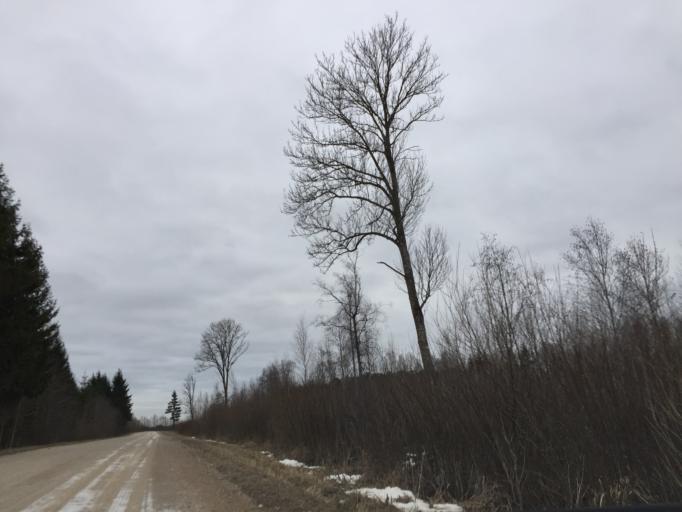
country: LT
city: Zagare
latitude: 56.3023
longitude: 23.2601
